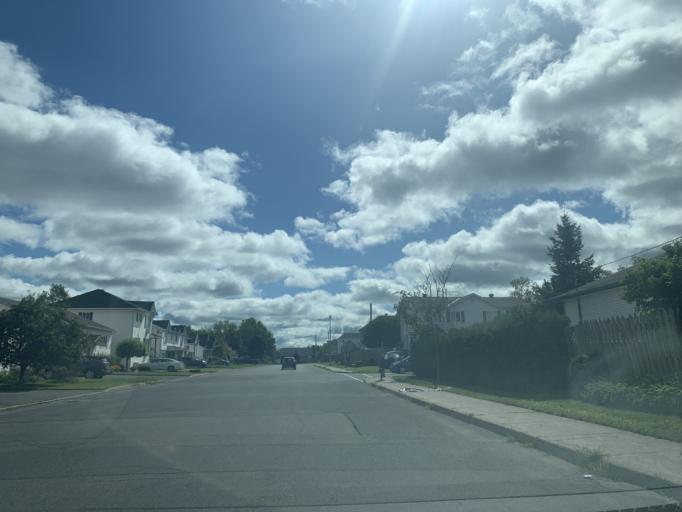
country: CA
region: Ontario
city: Hawkesbury
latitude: 45.6047
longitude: -74.5835
